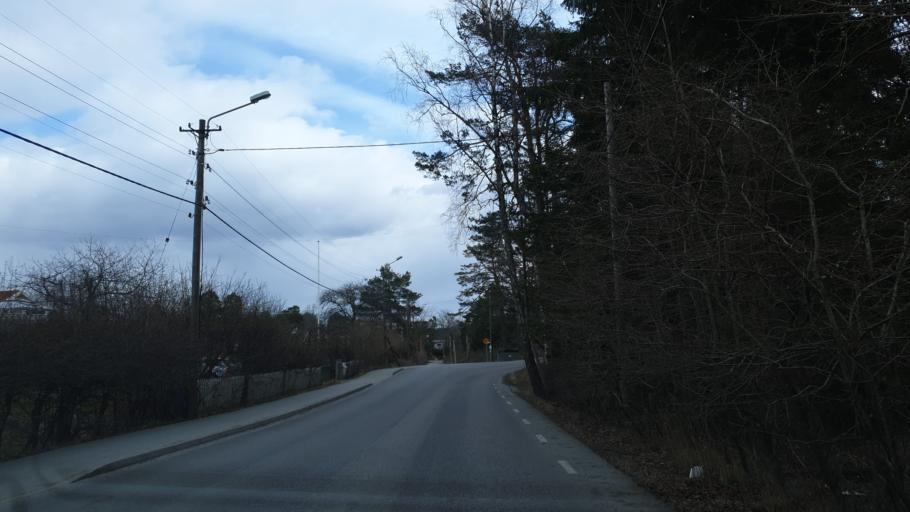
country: SE
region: Stockholm
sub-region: Nacka Kommun
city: Boo
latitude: 59.3237
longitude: 18.3019
